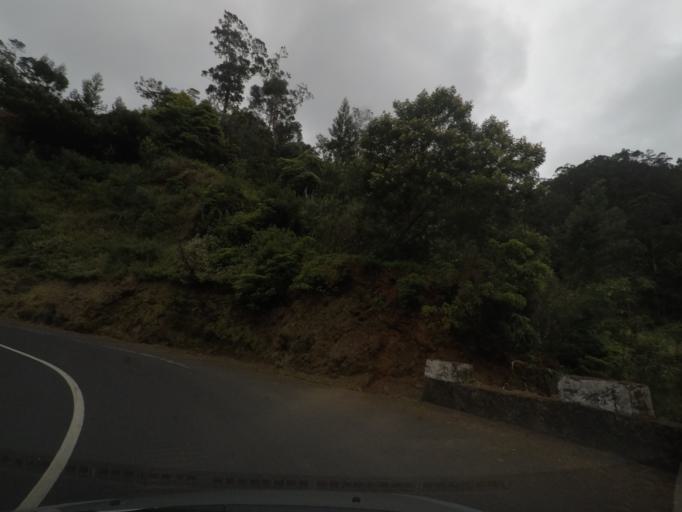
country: PT
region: Madeira
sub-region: Santana
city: Santana
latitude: 32.7508
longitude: -16.8399
